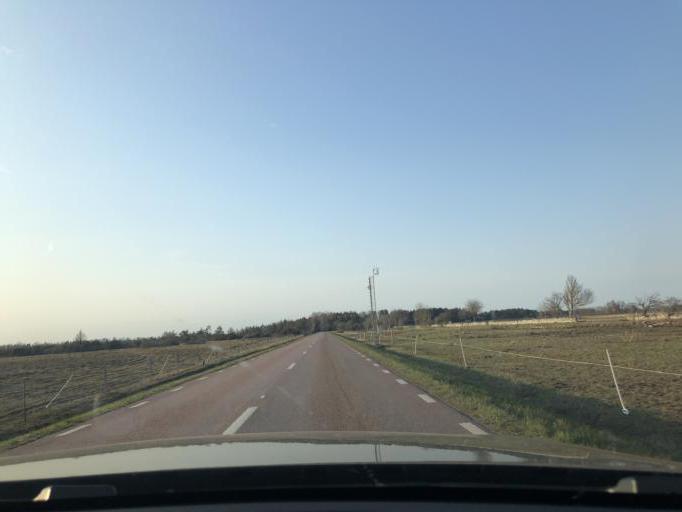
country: SE
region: Kalmar
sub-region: Morbylanga Kommun
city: Sodra Sandby
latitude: 56.5688
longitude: 16.6186
